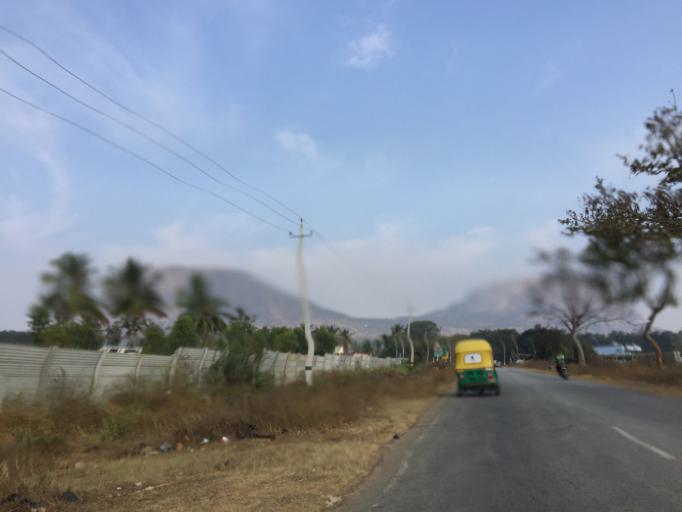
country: IN
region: Karnataka
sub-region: Bangalore Rural
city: Devanhalli
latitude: 13.3371
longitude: 77.6893
